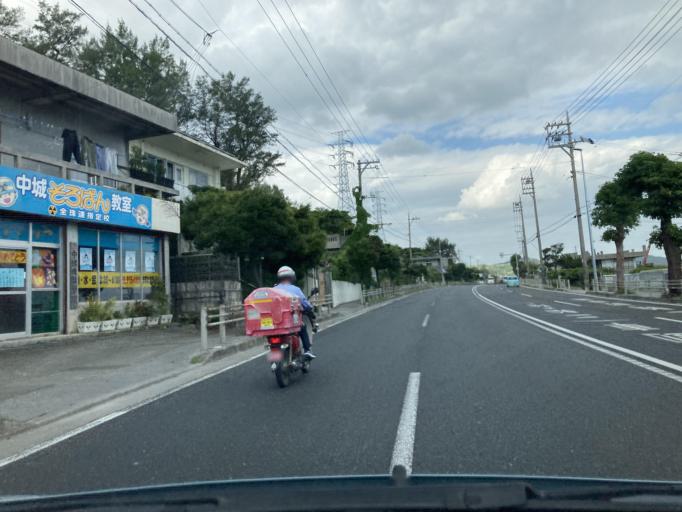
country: JP
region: Okinawa
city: Ginowan
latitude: 26.2494
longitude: 127.7824
